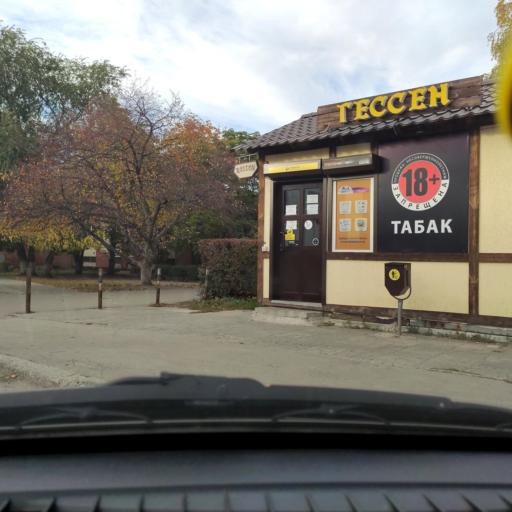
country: RU
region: Samara
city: Tol'yatti
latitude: 53.5069
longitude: 49.2830
